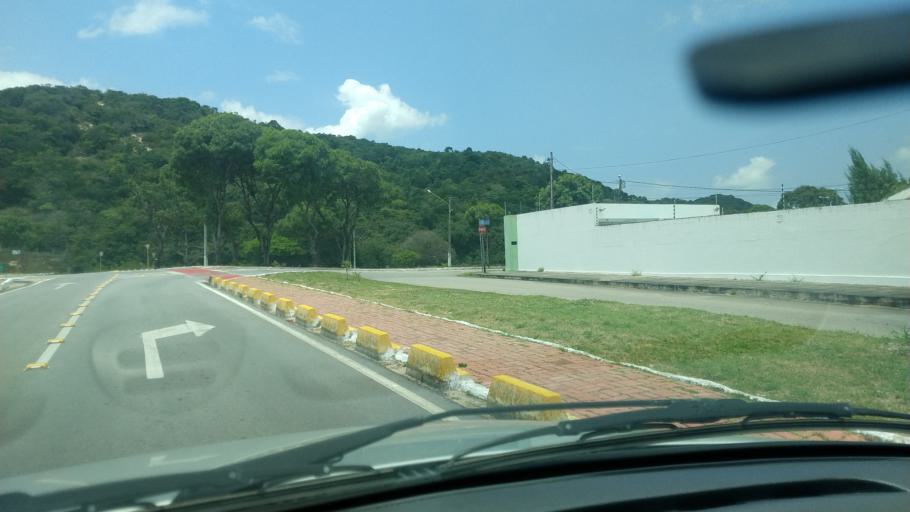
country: BR
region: Rio Grande do Norte
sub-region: Natal
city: Natal
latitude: -5.8441
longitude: -35.1970
